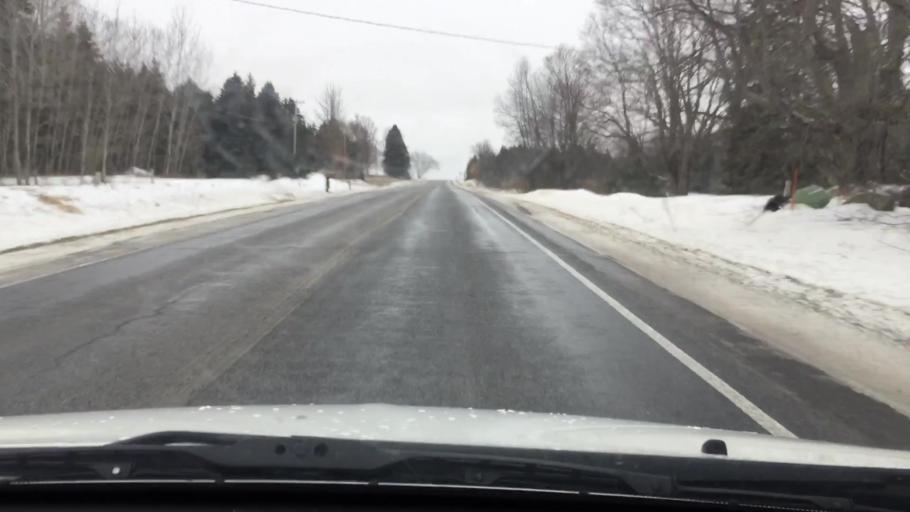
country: US
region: Michigan
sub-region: Osceola County
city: Reed City
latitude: 44.0484
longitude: -85.4439
